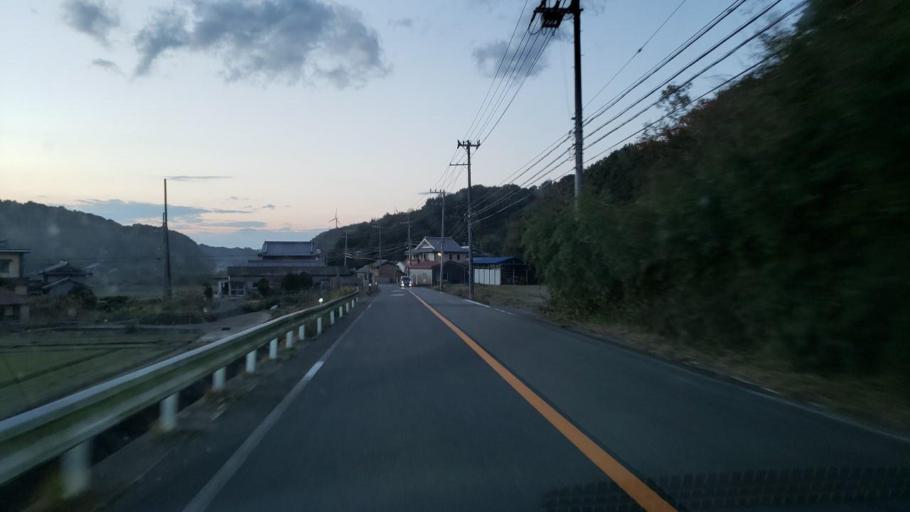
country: JP
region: Hyogo
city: Fukura
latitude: 34.2810
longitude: 134.6985
